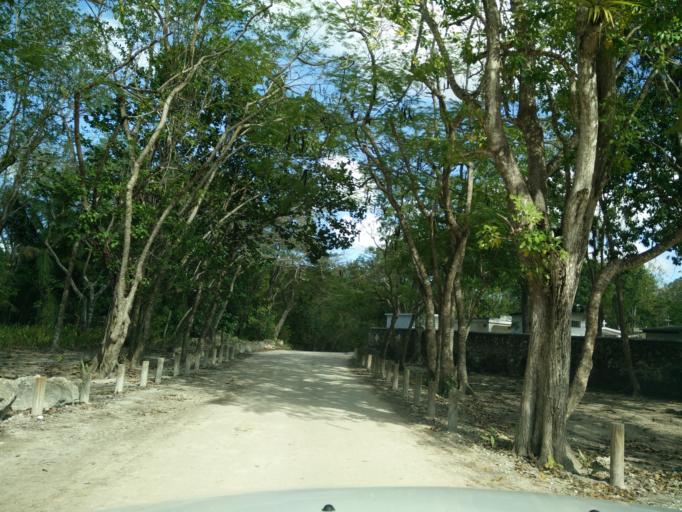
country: GP
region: Guadeloupe
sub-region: Guadeloupe
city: Port-Louis
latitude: 16.4266
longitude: -61.5338
